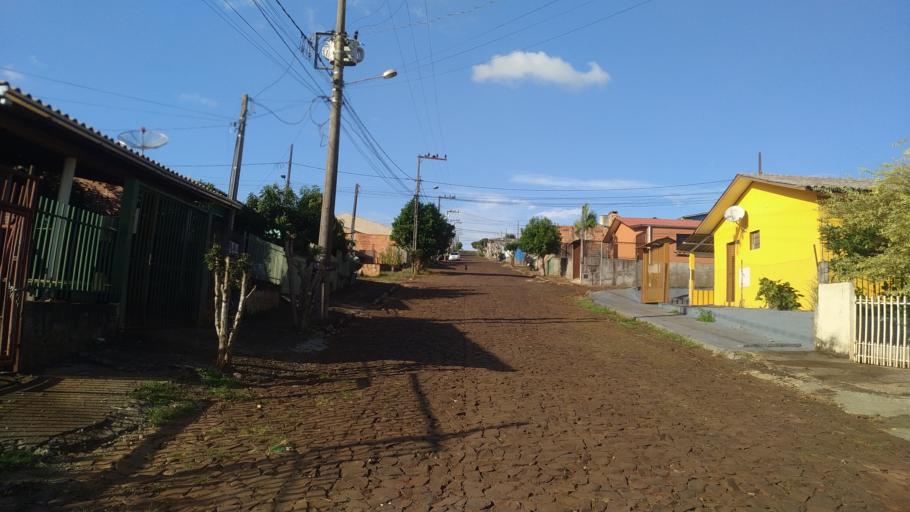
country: BR
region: Santa Catarina
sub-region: Chapeco
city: Chapeco
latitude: -27.0665
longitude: -52.6088
